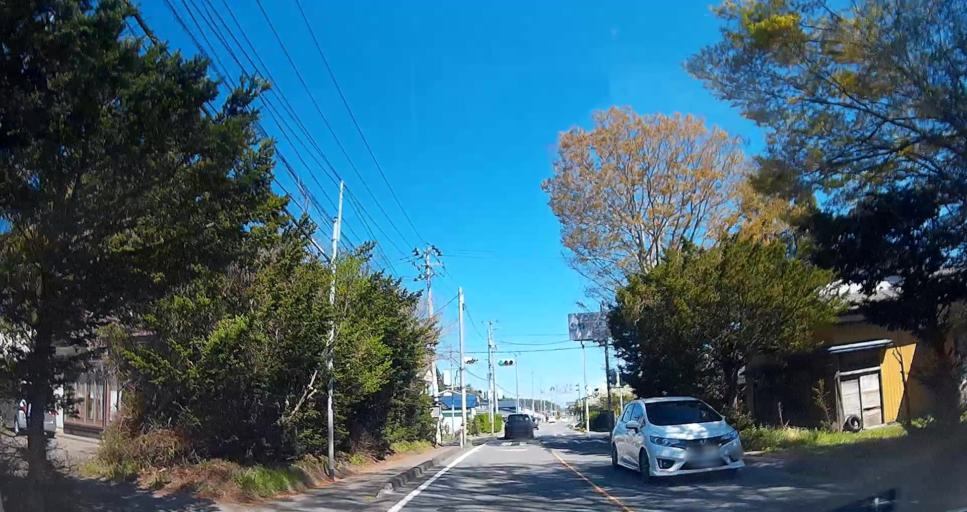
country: JP
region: Aomori
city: Misawa
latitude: 40.7353
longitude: 141.4111
